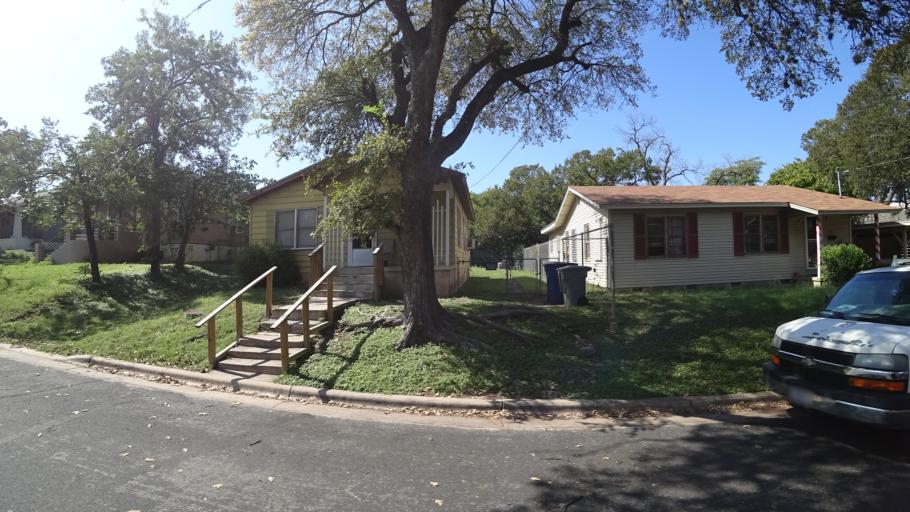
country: US
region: Texas
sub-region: Travis County
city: Austin
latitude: 30.2688
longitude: -97.7212
